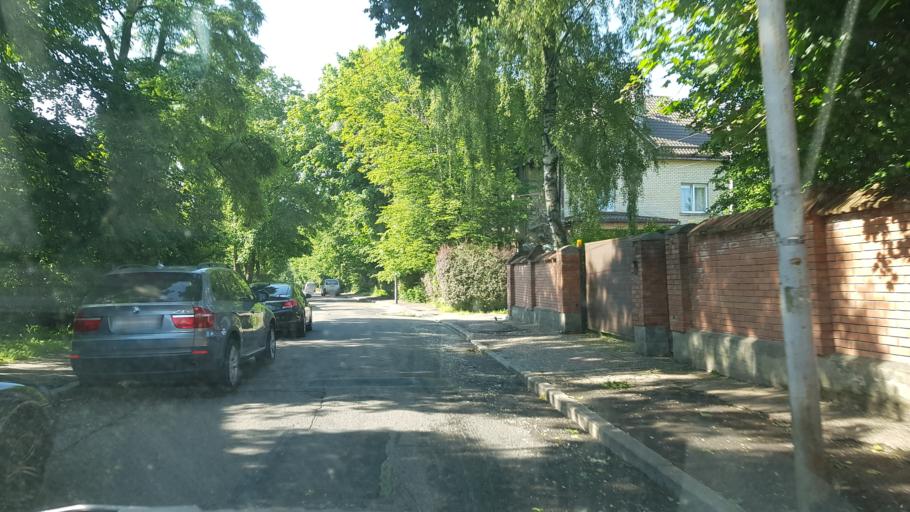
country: RU
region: Kaliningrad
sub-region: Gorod Kaliningrad
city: Kaliningrad
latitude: 54.7175
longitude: 20.4571
